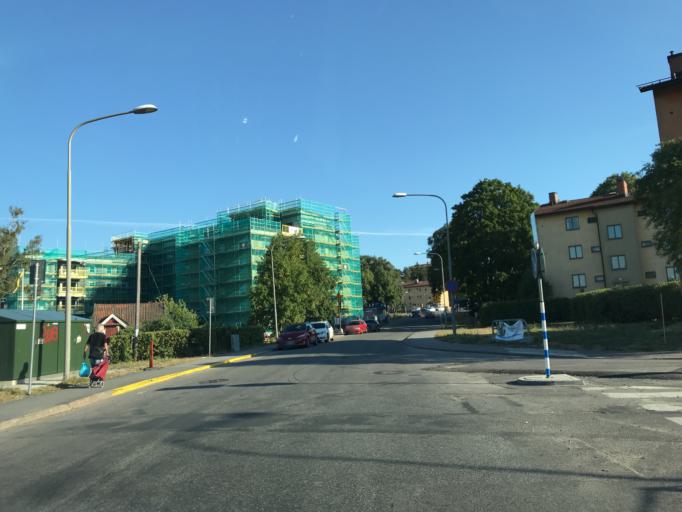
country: SE
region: Stockholm
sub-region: Stockholms Kommun
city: Bromma
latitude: 59.3391
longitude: 17.9525
